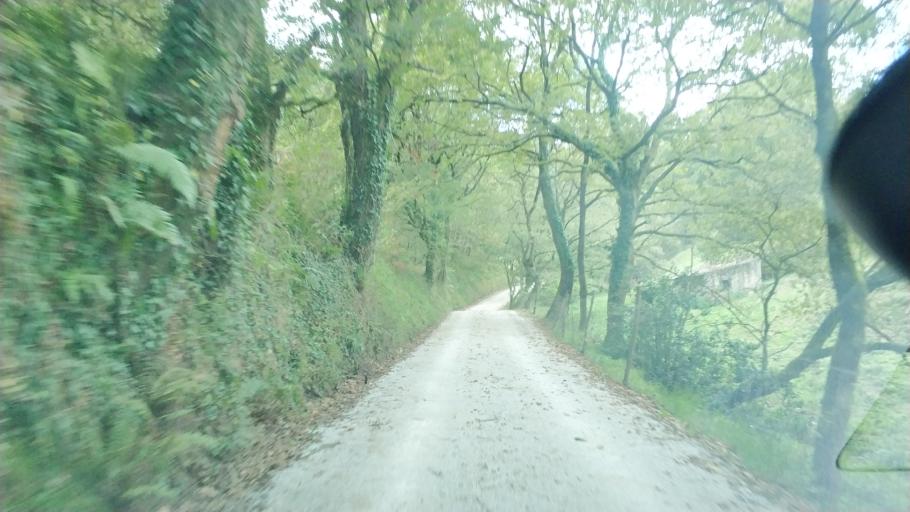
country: ES
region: Cantabria
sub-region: Provincia de Cantabria
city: Santa Maria de Cayon
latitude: 43.2952
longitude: -3.8550
